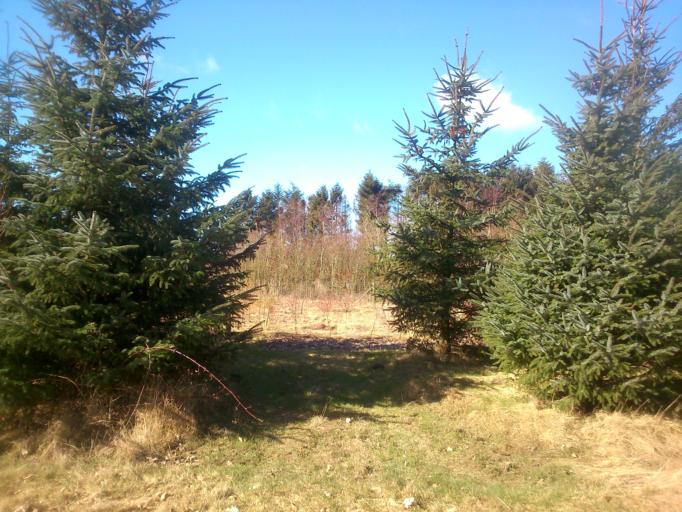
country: DK
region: Central Jutland
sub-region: Ringkobing-Skjern Kommune
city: Skjern
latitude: 55.9668
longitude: 8.4512
